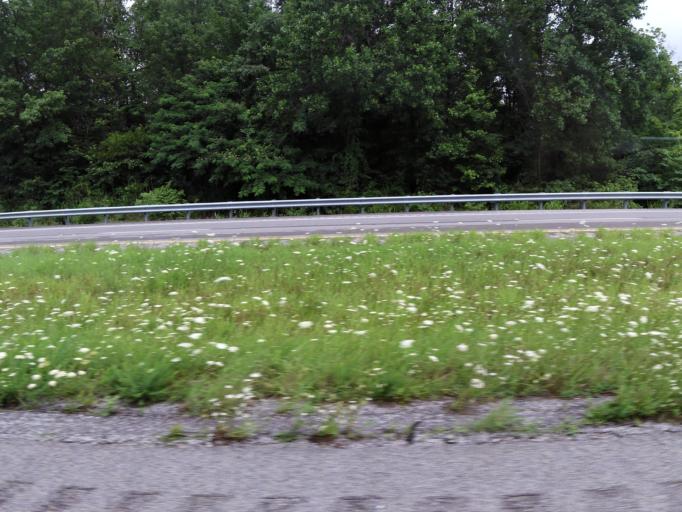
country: US
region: Kentucky
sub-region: Muhlenberg County
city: Central City
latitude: 37.3188
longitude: -87.0395
